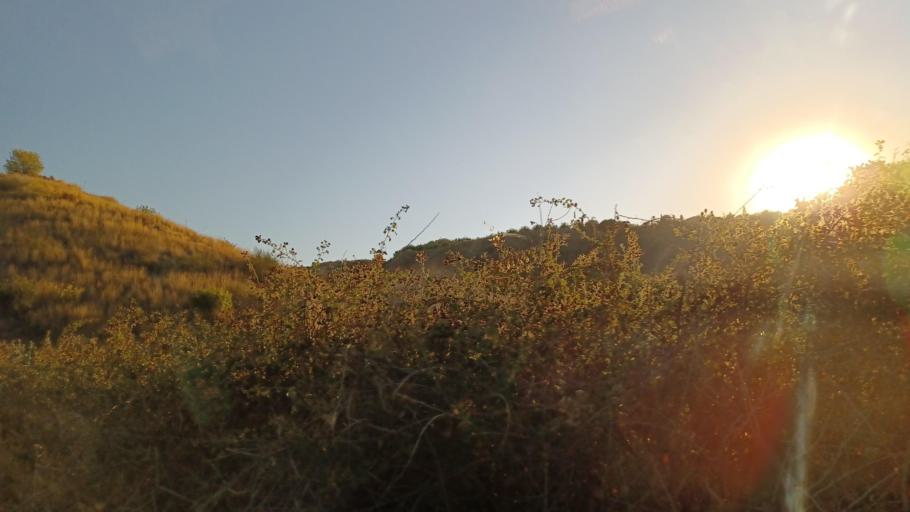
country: CY
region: Pafos
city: Polis
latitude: 34.9837
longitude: 32.4630
